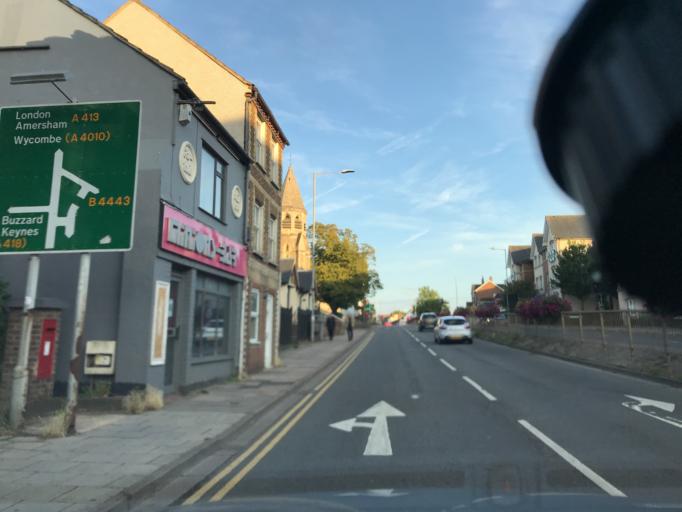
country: GB
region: England
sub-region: Buckinghamshire
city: Aylesbury
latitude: 51.8129
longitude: -0.8086
